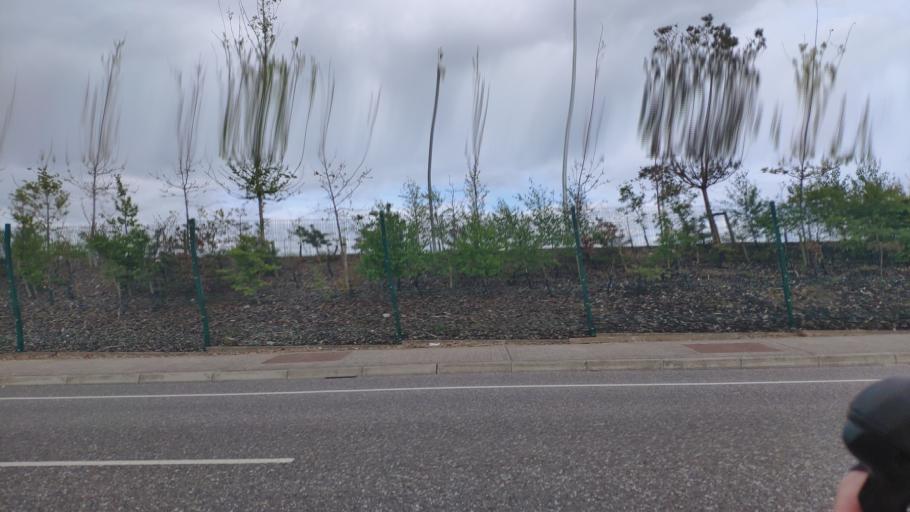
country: IE
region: Munster
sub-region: County Cork
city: Cork
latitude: 51.9061
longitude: -8.5184
